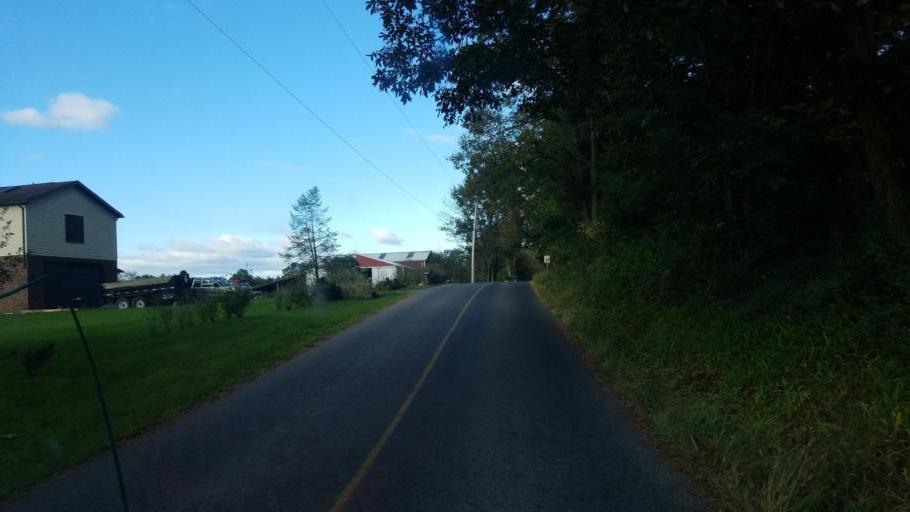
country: US
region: Pennsylvania
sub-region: Adams County
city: Biglerville
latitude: 39.8832
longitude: -77.3224
